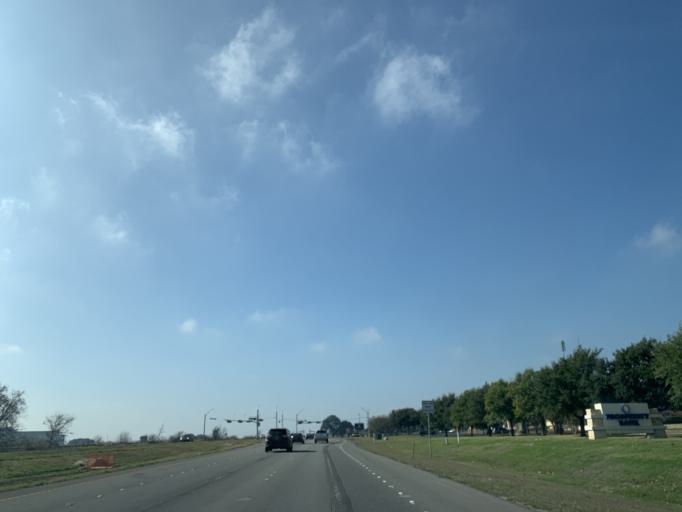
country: US
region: Texas
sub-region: Williamson County
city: Round Rock
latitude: 30.5272
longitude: -97.6274
